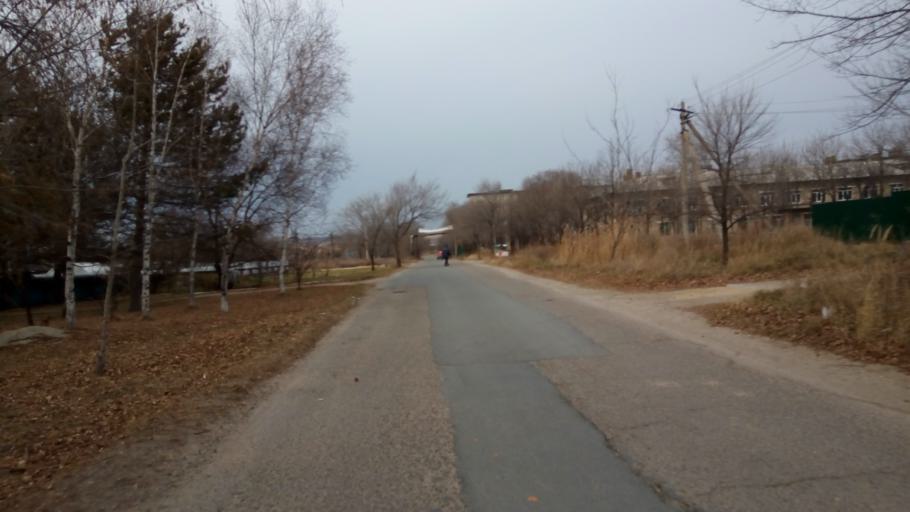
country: RU
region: Primorskiy
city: Novoshakhtinskiy
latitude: 44.0239
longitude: 132.1620
